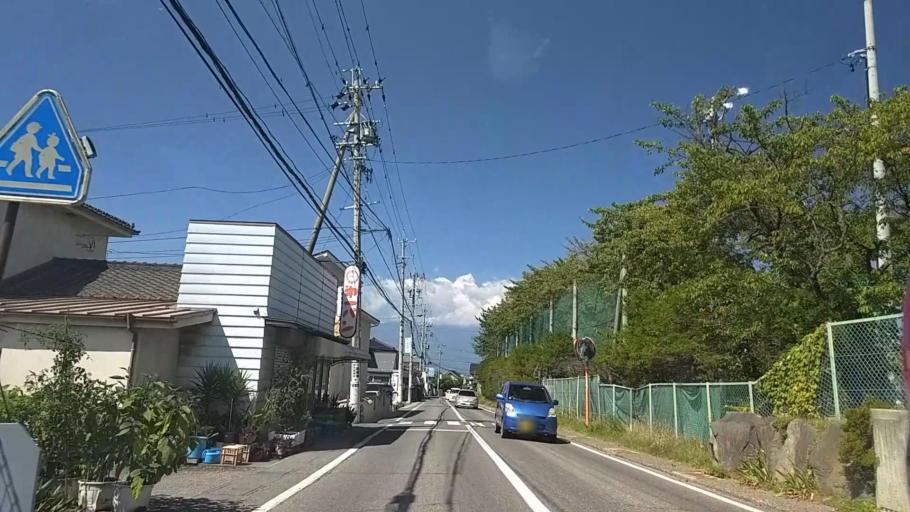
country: JP
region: Nagano
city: Matsumoto
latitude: 36.2370
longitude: 137.9940
